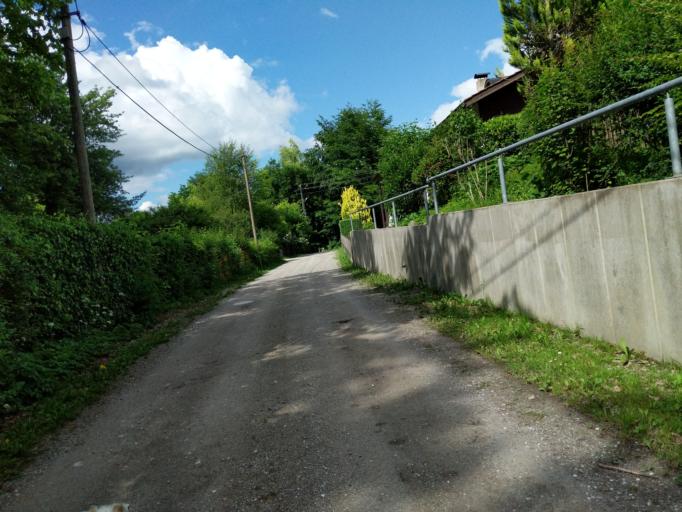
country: DE
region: Bavaria
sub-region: Upper Bavaria
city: Seefeld
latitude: 48.0176
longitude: 11.1977
